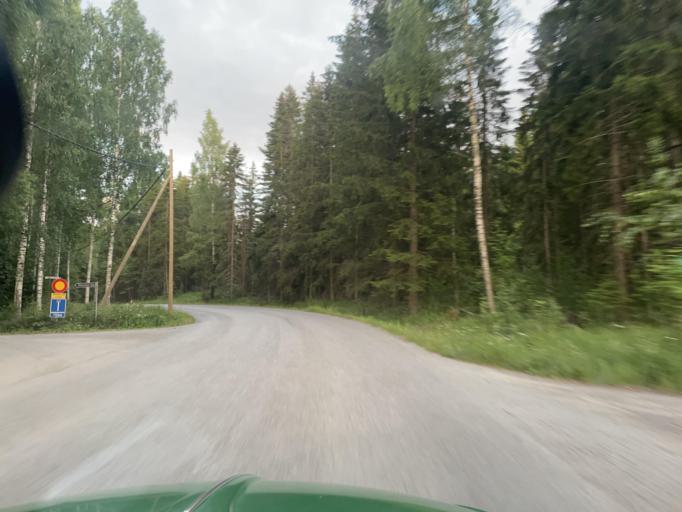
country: FI
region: Uusimaa
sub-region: Helsinki
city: Lohja
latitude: 60.2330
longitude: 24.0706
